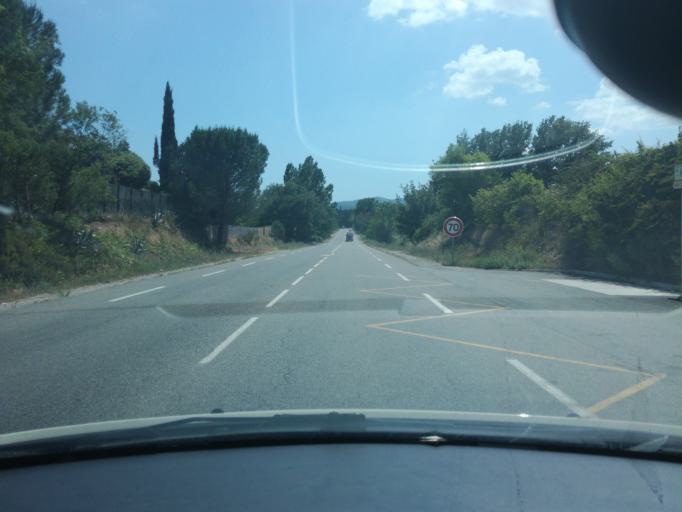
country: FR
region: Provence-Alpes-Cote d'Azur
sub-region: Departement du Var
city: Le Muy
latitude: 43.4845
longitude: 6.5668
